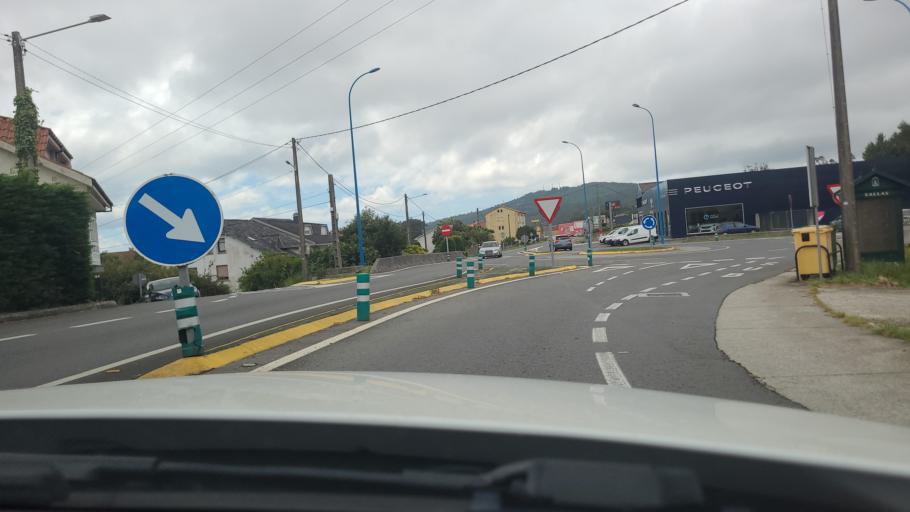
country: ES
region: Galicia
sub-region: Provincia da Coruna
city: Cee
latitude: 42.9724
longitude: -9.1902
